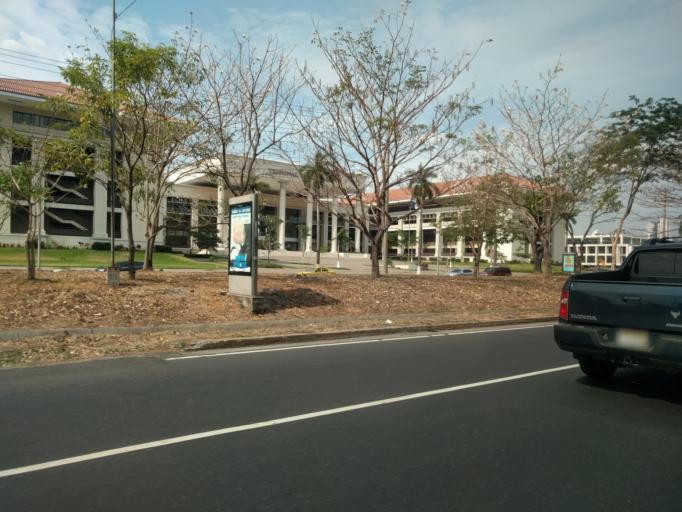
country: PA
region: Panama
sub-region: Distrito de Panama
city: Ancon
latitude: 8.9657
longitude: -79.5489
